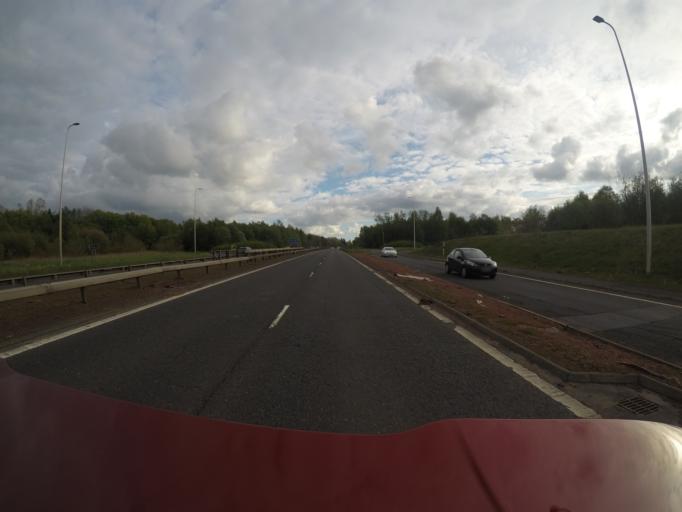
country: GB
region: Scotland
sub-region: West Dunbartonshire
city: Old Kilpatrick
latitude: 55.9106
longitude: -4.4727
